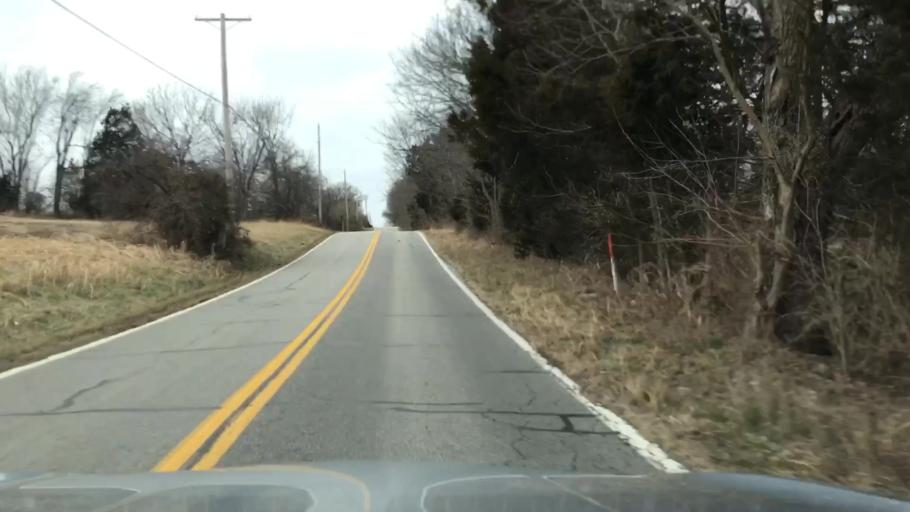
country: US
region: Missouri
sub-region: Jackson County
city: Lees Summit
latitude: 38.8899
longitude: -94.4080
